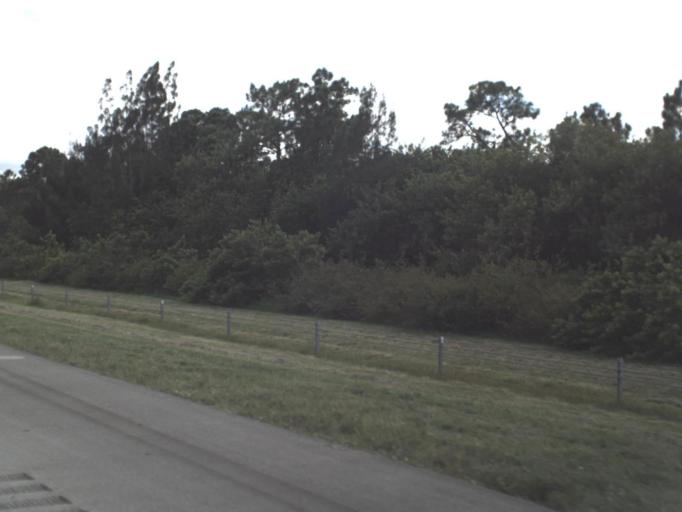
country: US
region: Florida
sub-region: Saint Lucie County
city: Lakewood Park
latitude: 27.4593
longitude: -80.4323
